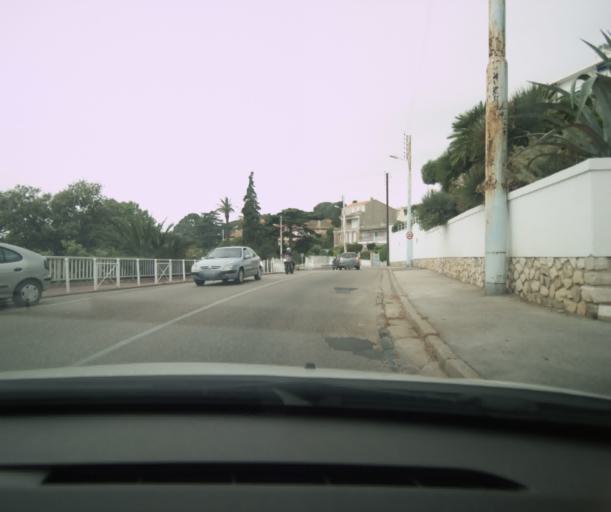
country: FR
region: Provence-Alpes-Cote d'Azur
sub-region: Departement du Var
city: Toulon
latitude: 43.1085
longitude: 5.9513
